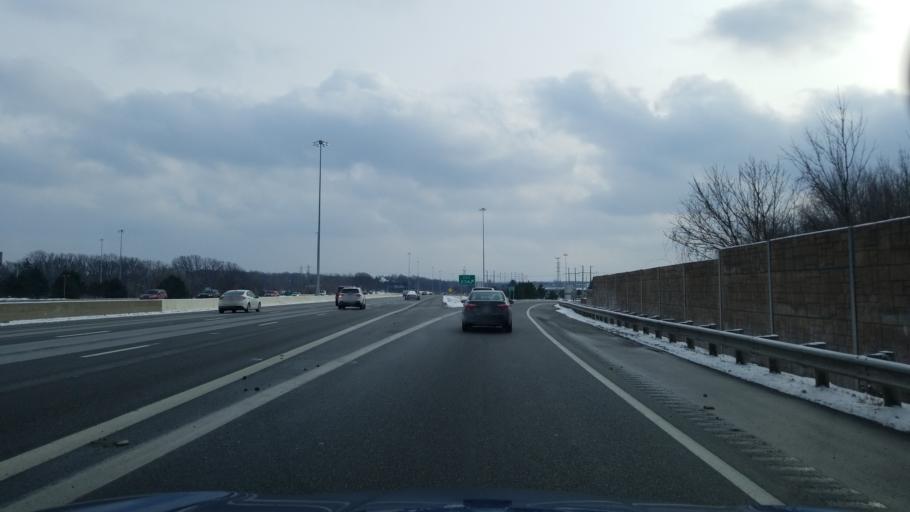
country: US
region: Ohio
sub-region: Cuyahoga County
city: Middleburg Heights
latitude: 41.3584
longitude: -81.8202
